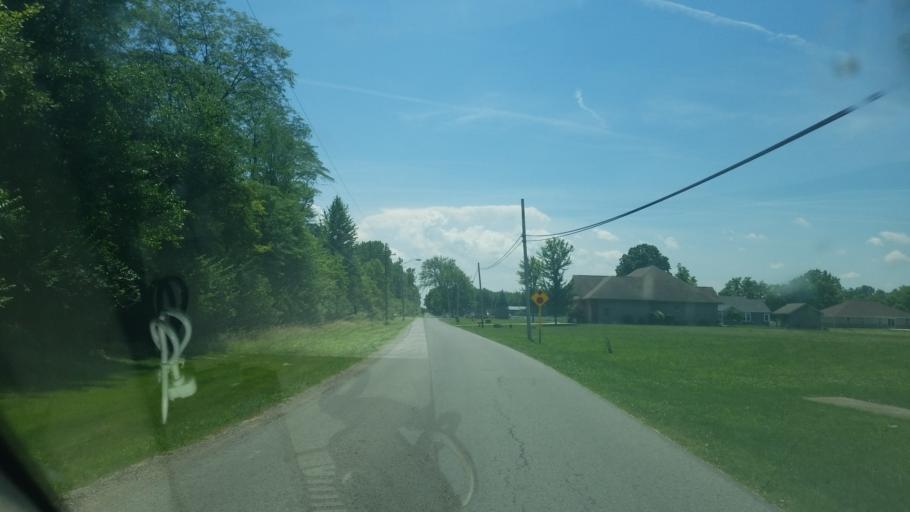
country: US
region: Ohio
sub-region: Hancock County
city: Findlay
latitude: 41.0098
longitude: -83.6363
